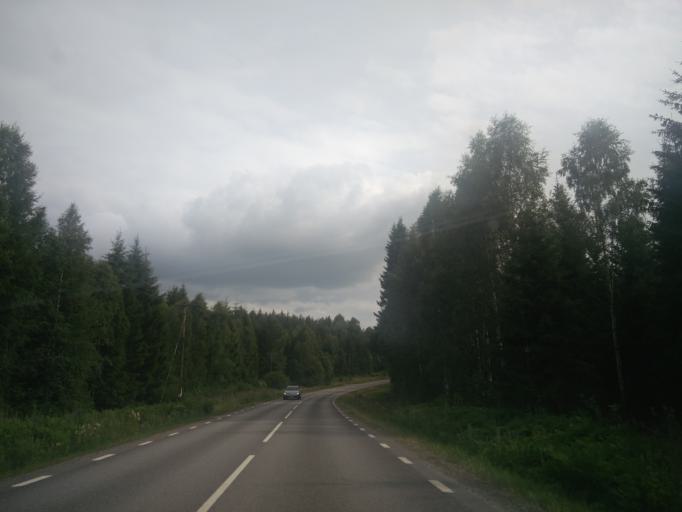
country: SE
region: Vaermland
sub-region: Arvika Kommun
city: Arvika
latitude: 59.7307
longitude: 12.5640
